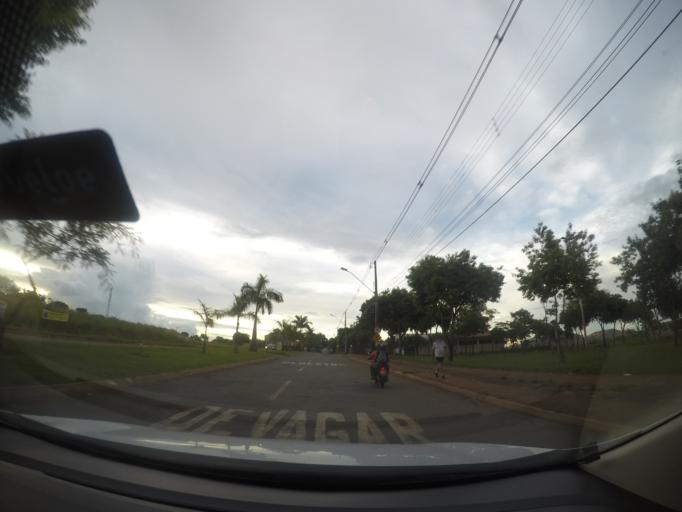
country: BR
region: Goias
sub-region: Goiania
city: Goiania
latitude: -16.7257
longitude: -49.3714
